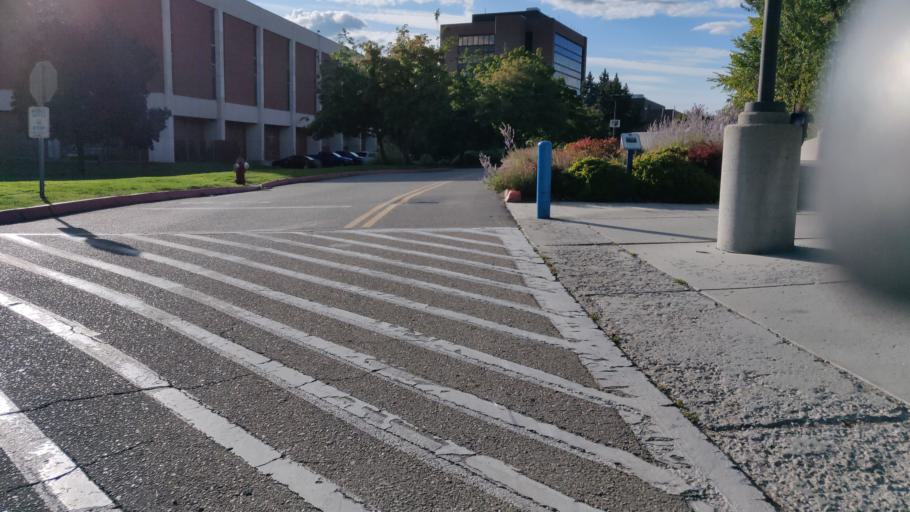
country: US
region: Idaho
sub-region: Ada County
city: Boise
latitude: 43.6049
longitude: -116.2035
